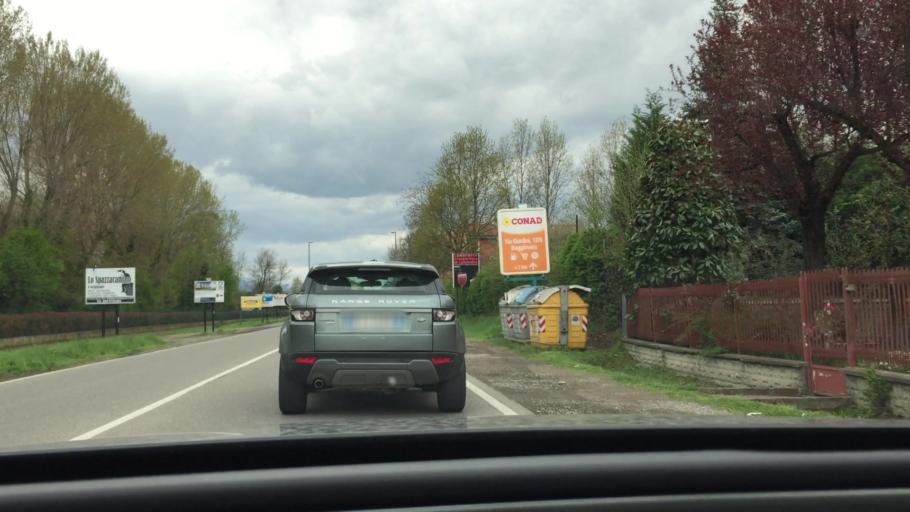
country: IT
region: Emilia-Romagna
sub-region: Provincia di Modena
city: Baggiovara
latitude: 44.6248
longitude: 10.8942
